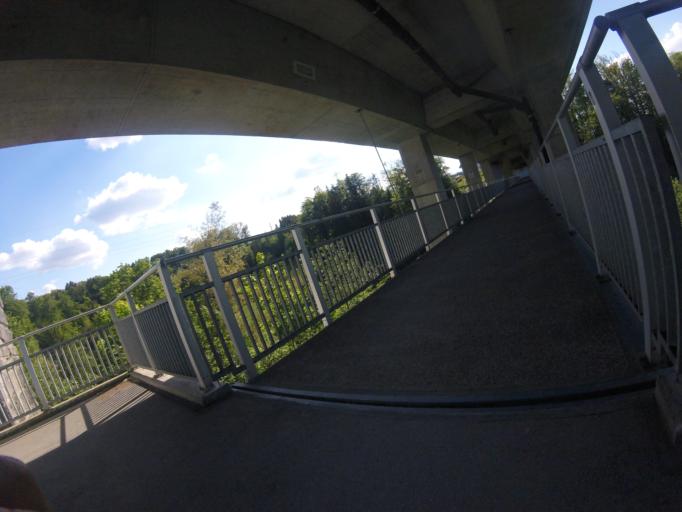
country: CH
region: Saint Gallen
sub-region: Wahlkreis St. Gallen
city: Gossau
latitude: 47.4068
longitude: 9.2189
